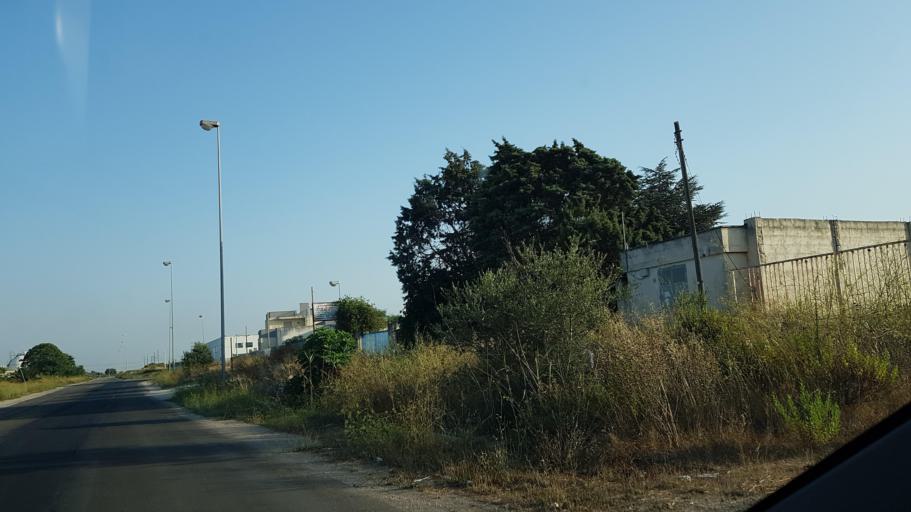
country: IT
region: Apulia
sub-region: Provincia di Brindisi
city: Materdomini
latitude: 40.6290
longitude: 17.9757
